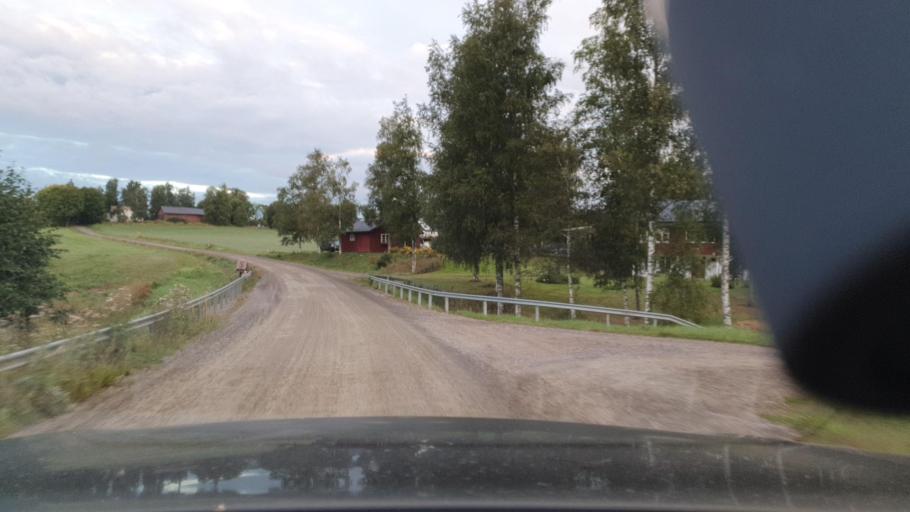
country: SE
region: Vaermland
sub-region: Sunne Kommun
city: Sunne
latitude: 59.8113
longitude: 13.0628
